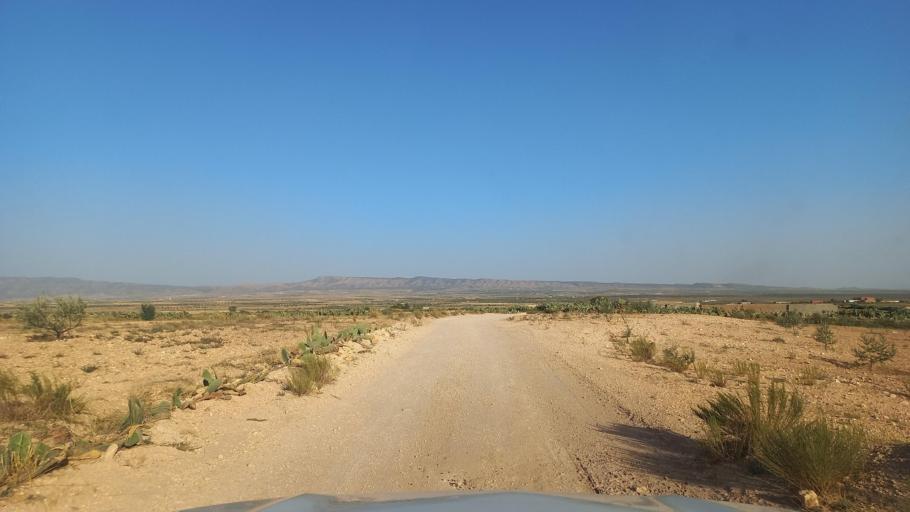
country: TN
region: Al Qasrayn
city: Sbiba
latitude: 35.3672
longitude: 9.0110
